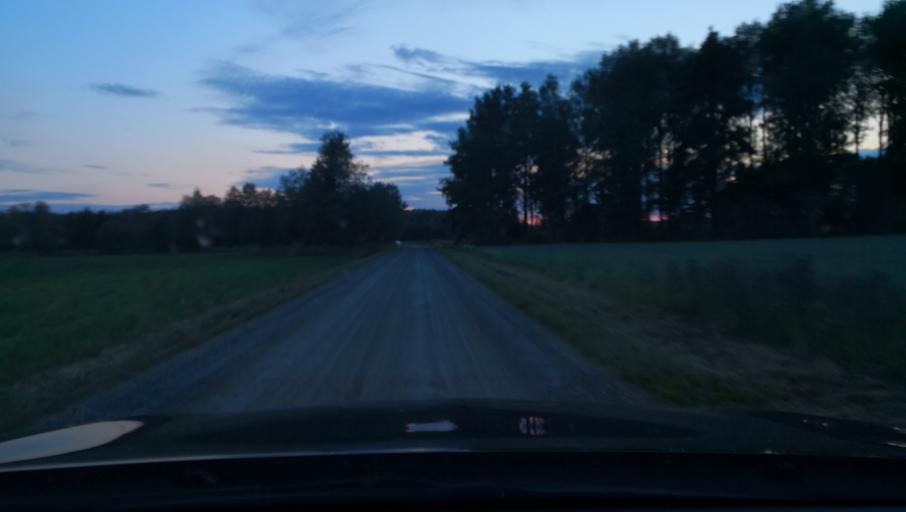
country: SE
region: Uppsala
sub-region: Osthammars Kommun
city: Bjorklinge
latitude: 60.0023
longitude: 17.3546
